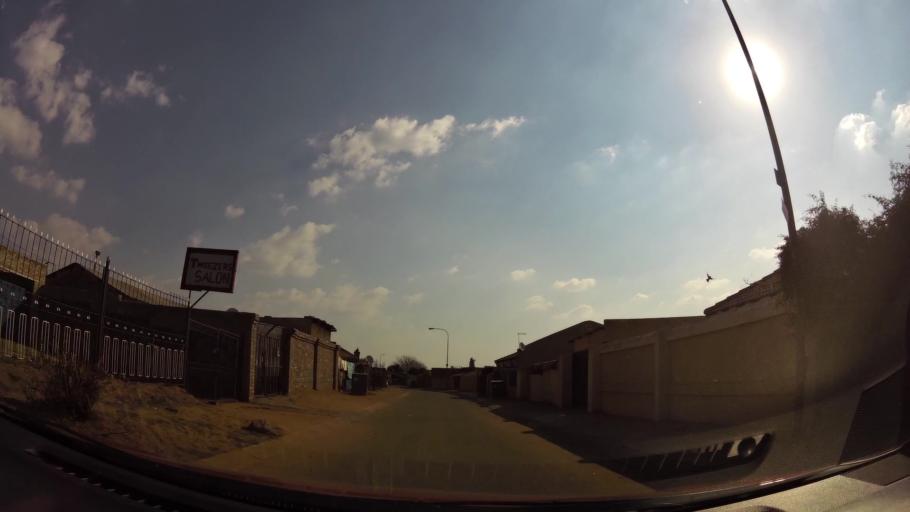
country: ZA
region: Gauteng
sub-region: City of Johannesburg Metropolitan Municipality
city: Soweto
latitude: -26.2372
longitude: 27.9496
